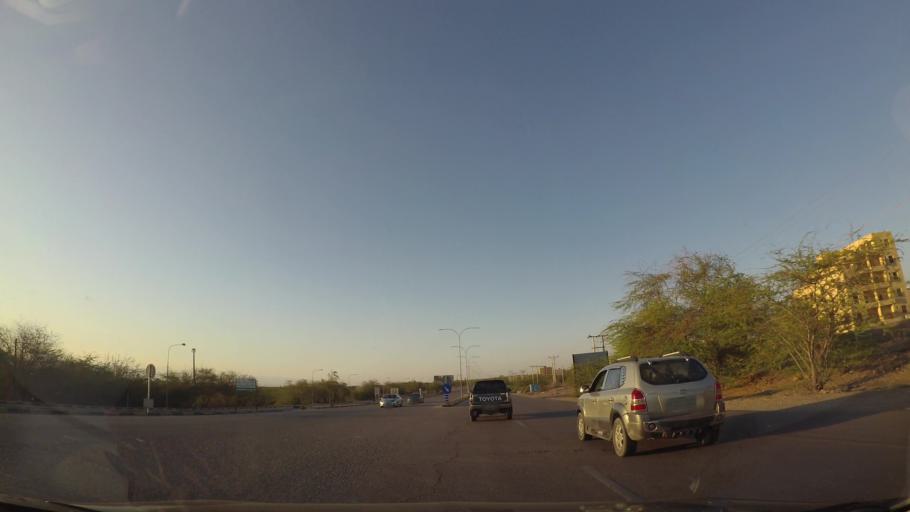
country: PS
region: West Bank
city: Jericho
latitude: 31.7566
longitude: 35.5936
